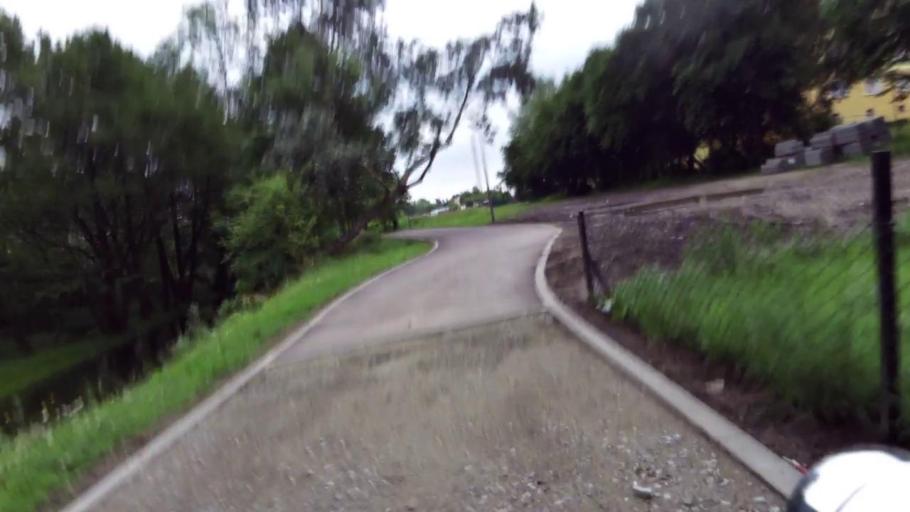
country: PL
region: West Pomeranian Voivodeship
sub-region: Koszalin
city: Koszalin
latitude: 54.1839
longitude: 16.1939
